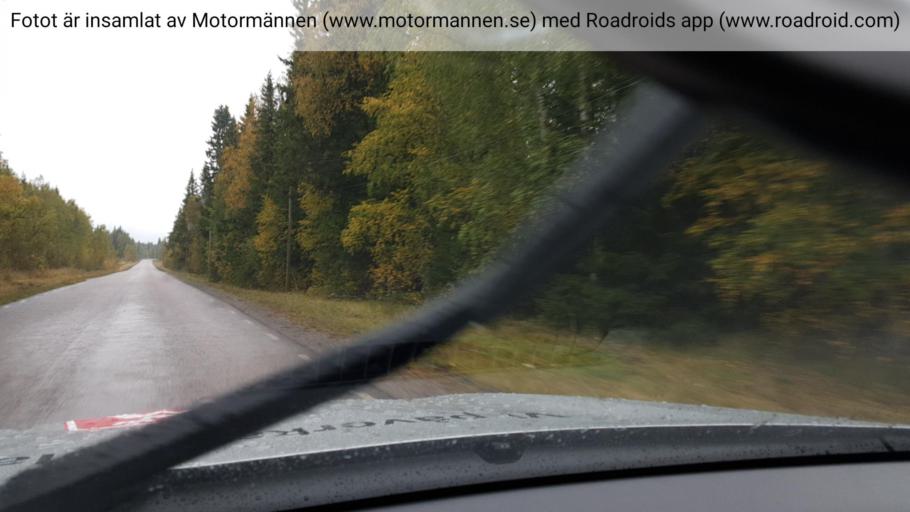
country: SE
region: Norrbotten
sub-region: Lulea Kommun
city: Gammelstad
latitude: 65.7408
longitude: 22.1139
